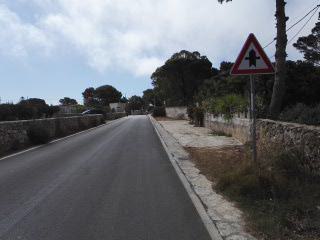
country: IT
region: Sicily
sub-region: Trapani
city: Favignana
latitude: 37.9212
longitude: 12.3437
